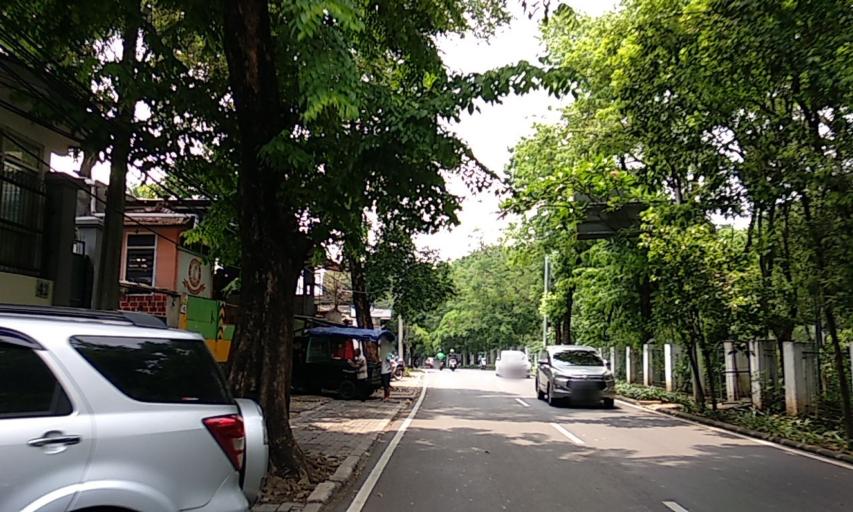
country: ID
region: Jakarta Raya
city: Jakarta
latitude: -6.2388
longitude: 106.8531
